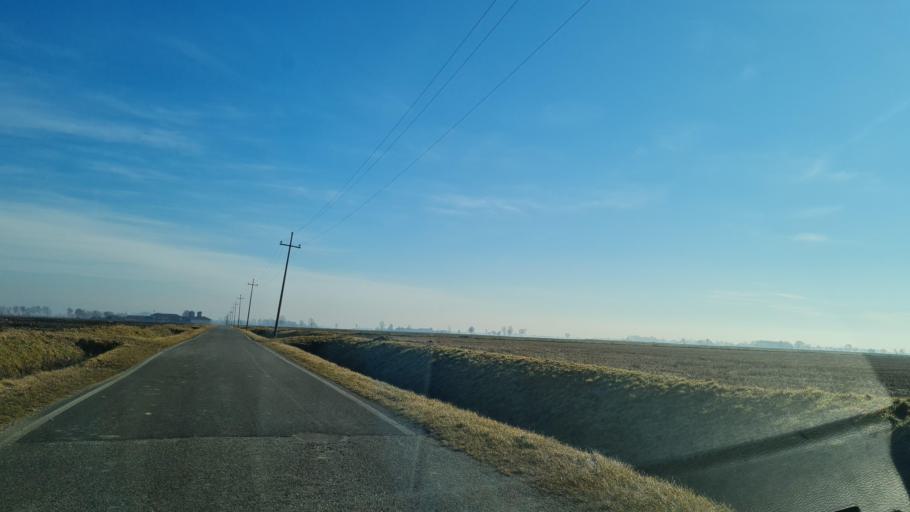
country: IT
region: Piedmont
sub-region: Provincia di Biella
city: Villanova Biellese
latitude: 45.4536
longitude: 8.1909
